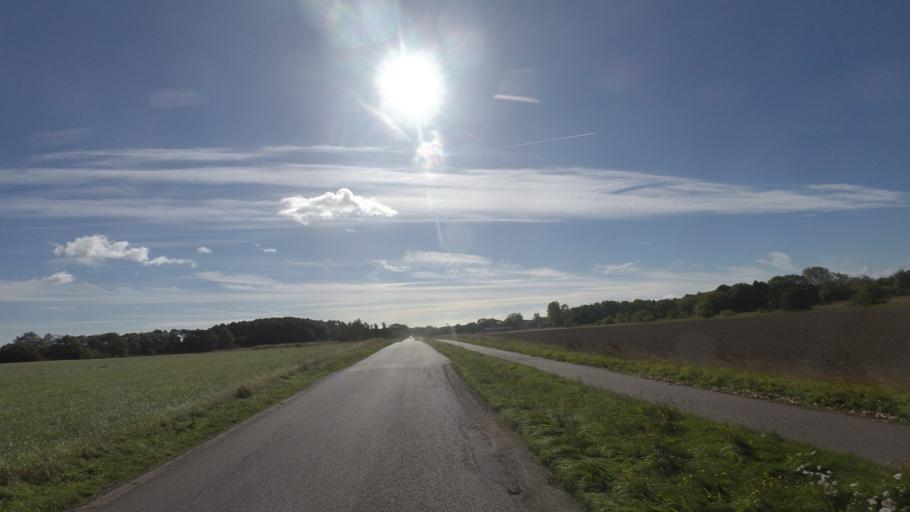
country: DK
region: Capital Region
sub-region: Bornholm Kommune
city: Akirkeby
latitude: 55.0130
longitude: 14.9912
